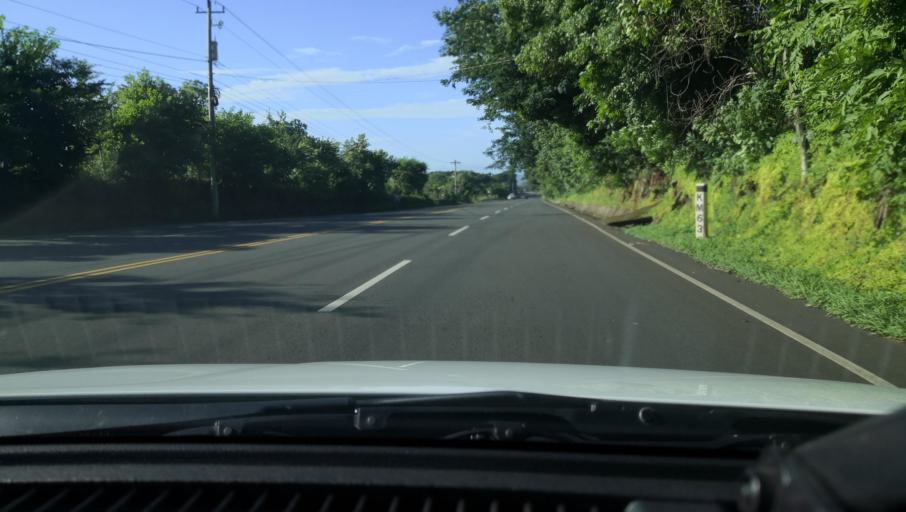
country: NI
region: Granada
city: Nandaime
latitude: 11.7849
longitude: -86.0563
